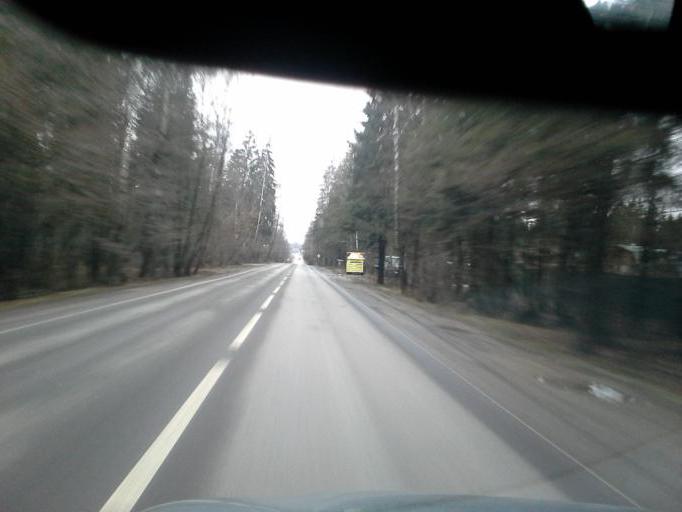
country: RU
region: Moskovskaya
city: Zhavoronki
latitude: 55.6318
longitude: 37.0986
